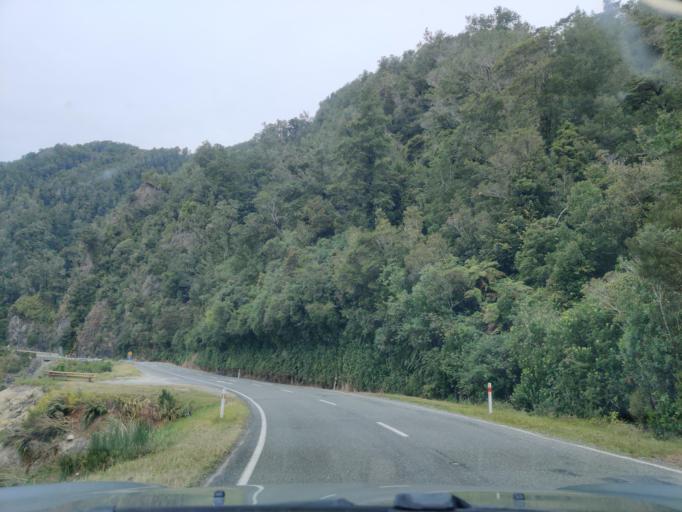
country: NZ
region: West Coast
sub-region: Buller District
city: Westport
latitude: -41.8640
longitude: 171.7766
